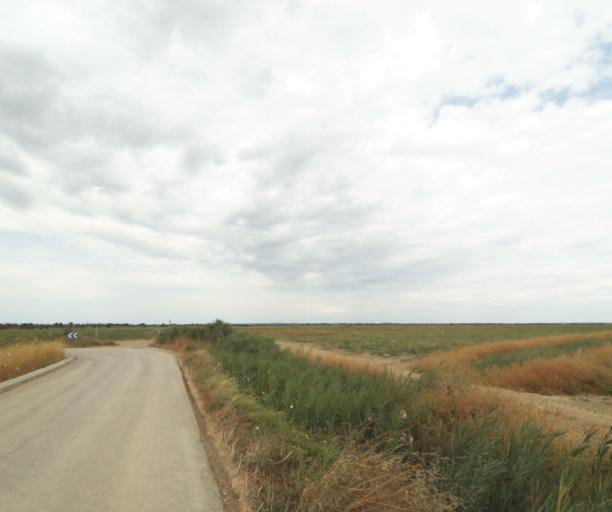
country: FR
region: Languedoc-Roussillon
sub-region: Departement de l'Herault
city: La Grande-Motte
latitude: 43.5965
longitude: 4.1089
